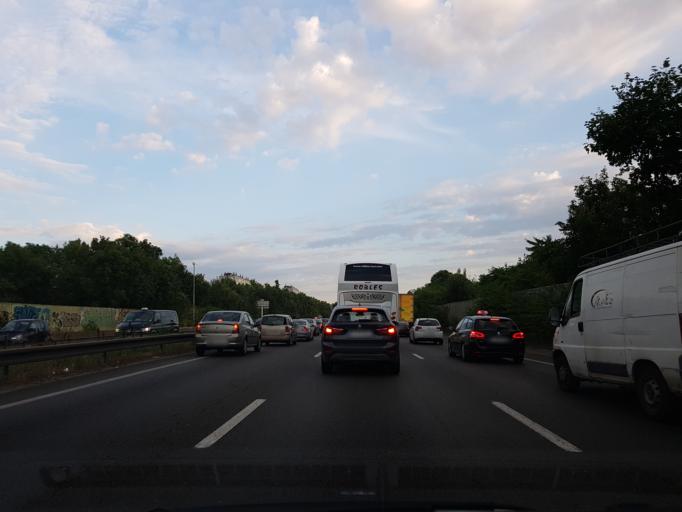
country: FR
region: Ile-de-France
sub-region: Departement de Seine-Saint-Denis
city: Bondy
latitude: 48.9186
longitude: 2.4786
